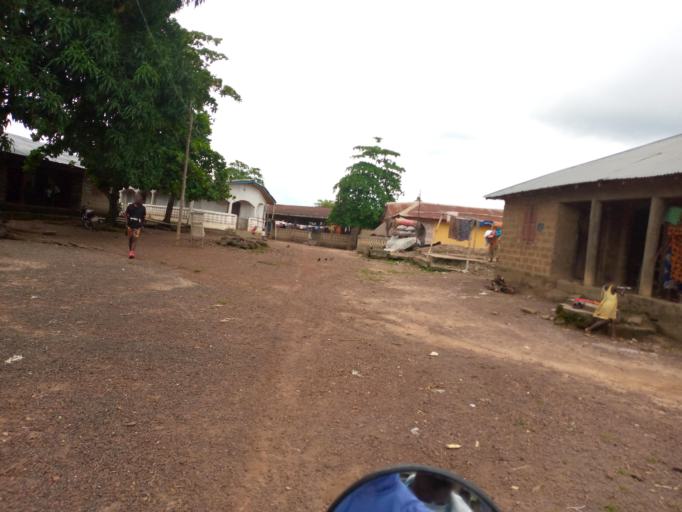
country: SL
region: Northern Province
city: Mange
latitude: 8.9873
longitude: -12.7180
